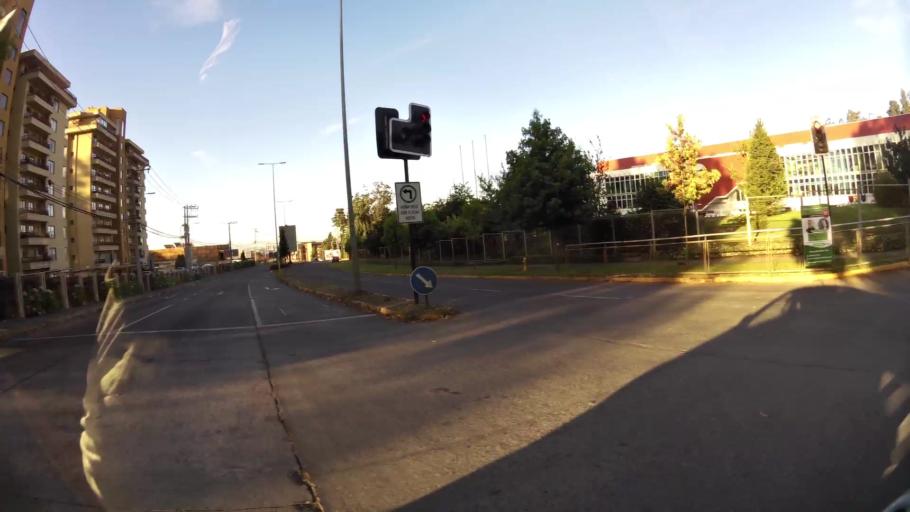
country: CL
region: Biobio
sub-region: Provincia de Concepcion
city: Concepcion
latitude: -36.8508
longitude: -73.0933
